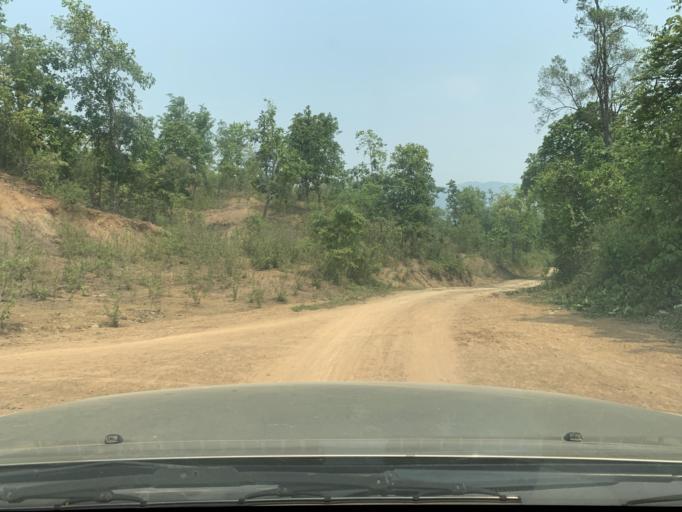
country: LA
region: Louangphabang
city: Louangphabang
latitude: 19.9430
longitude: 102.1331
